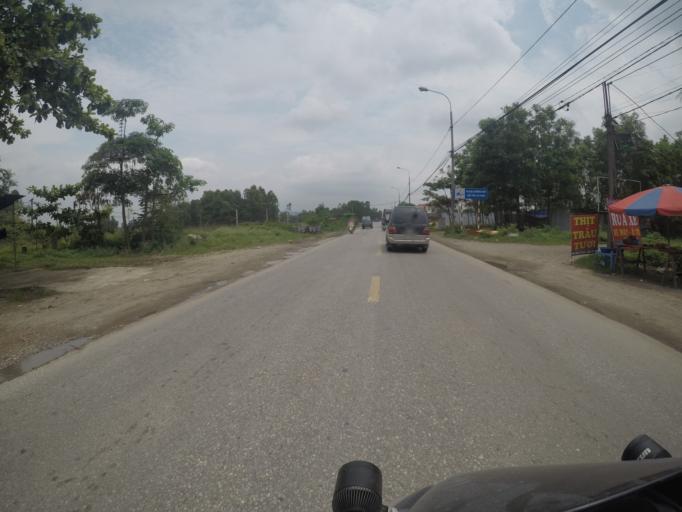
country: VN
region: Ha Noi
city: Soc Son
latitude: 21.2279
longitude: 105.8490
